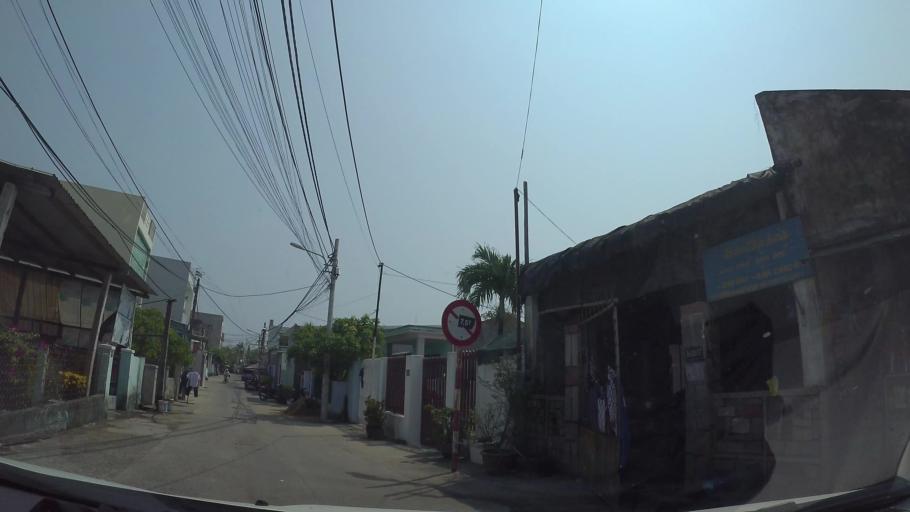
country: VN
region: Da Nang
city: Ngu Hanh Son
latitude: 16.0192
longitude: 108.2500
